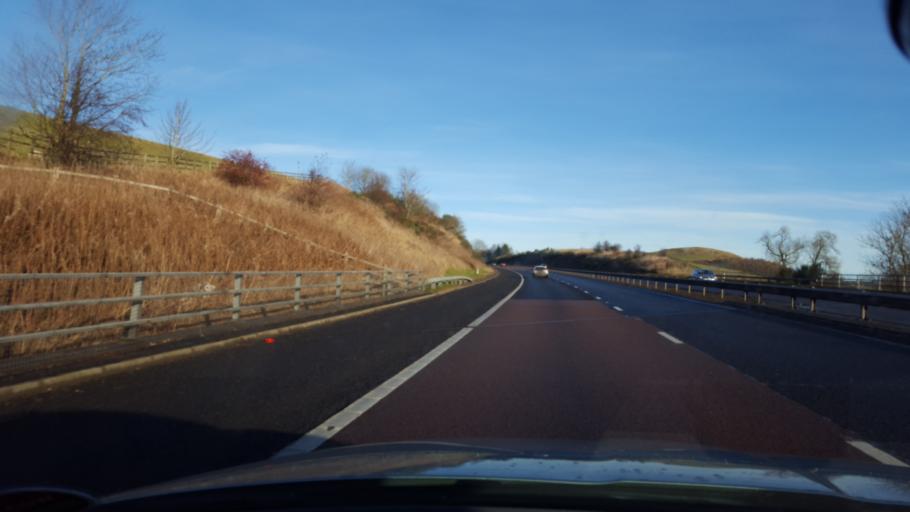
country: GB
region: Scotland
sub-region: Perth and Kinross
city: Bridge of Earn
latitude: 56.2943
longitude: -3.3860
